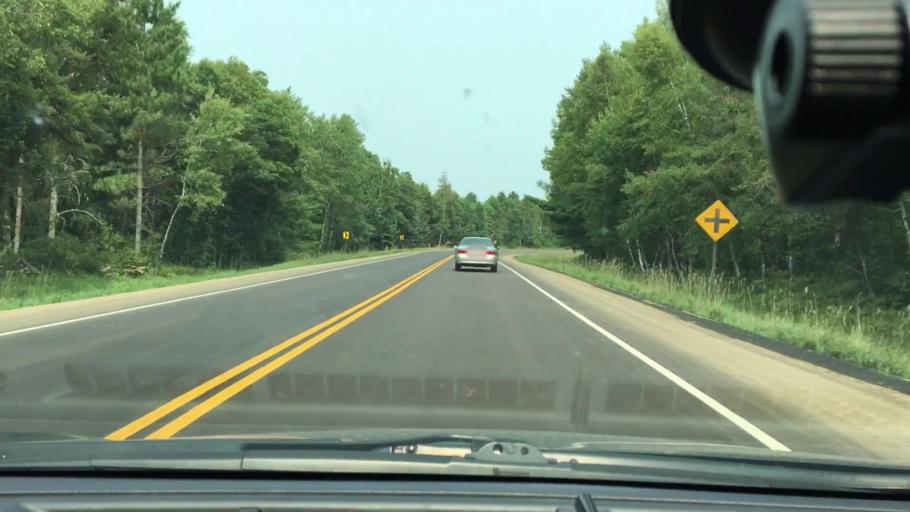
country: US
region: Minnesota
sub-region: Crow Wing County
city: Nisswa
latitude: 46.5267
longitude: -94.2690
